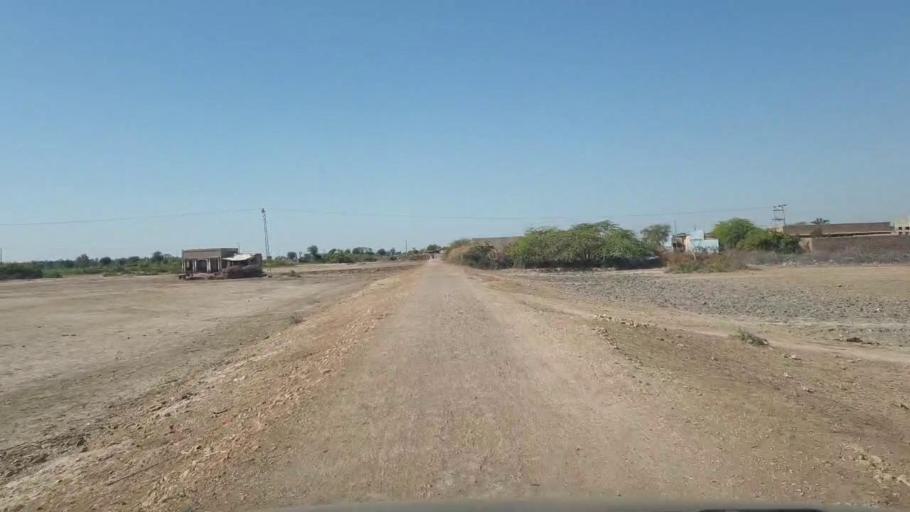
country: PK
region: Sindh
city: Dhoro Naro
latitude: 25.4072
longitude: 69.6093
